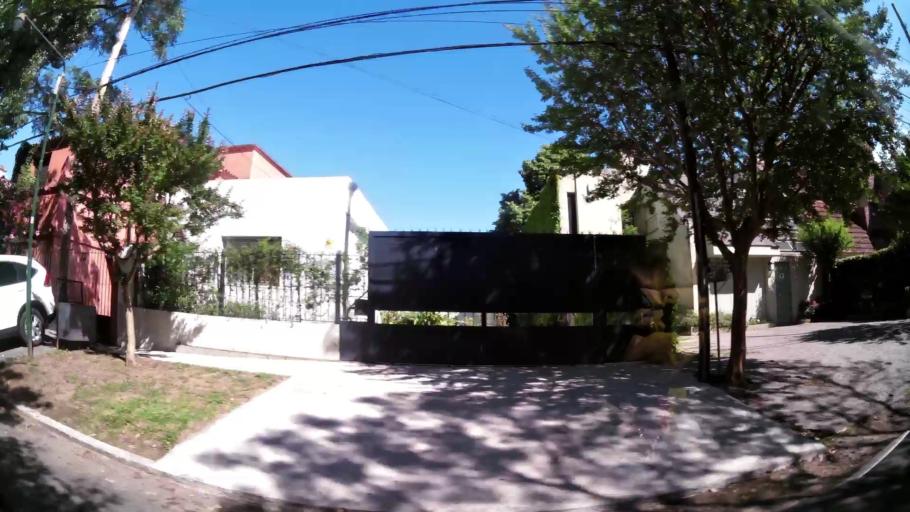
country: AR
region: Buenos Aires
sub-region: Partido de Tigre
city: Tigre
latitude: -34.4880
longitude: -58.5693
